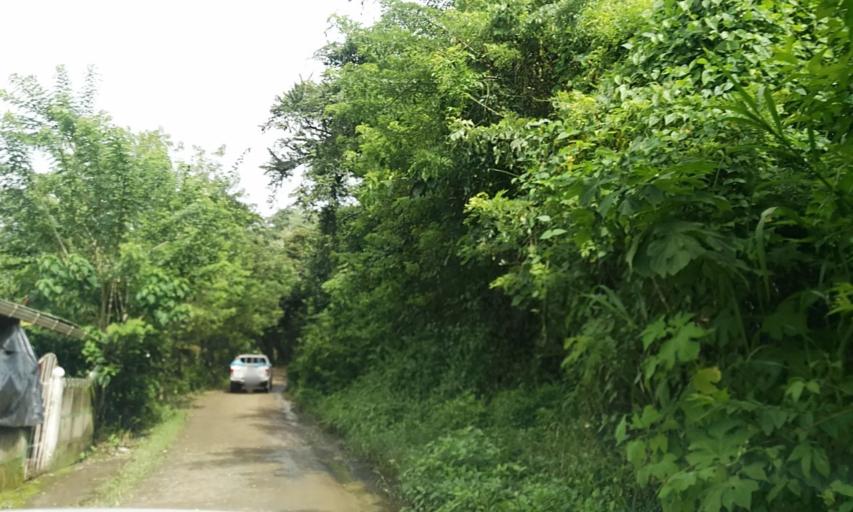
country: NI
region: Matagalpa
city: San Ramon
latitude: 12.9832
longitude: -85.8447
